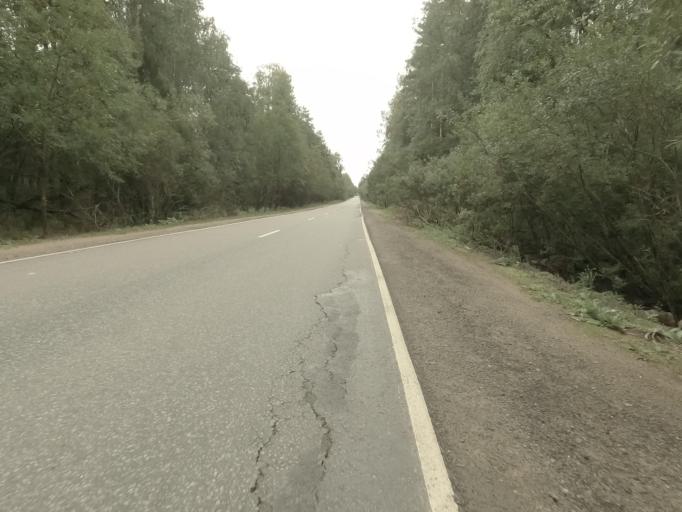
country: RU
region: Leningrad
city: Koltushi
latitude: 59.8991
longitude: 30.7627
